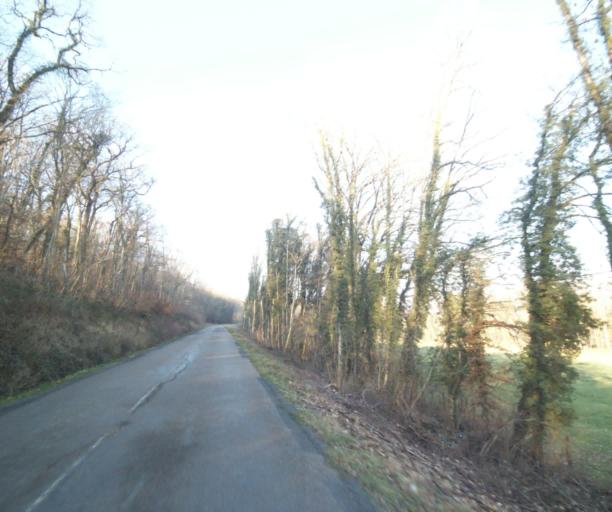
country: FR
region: Champagne-Ardenne
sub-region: Departement de la Haute-Marne
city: Bienville
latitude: 48.5678
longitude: 5.0794
